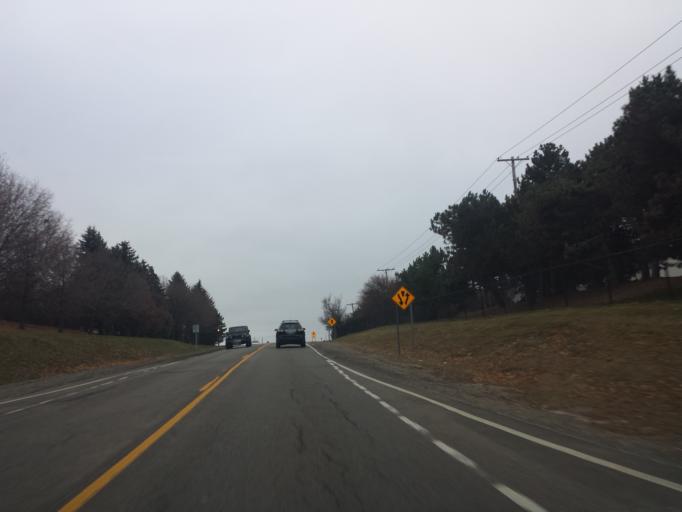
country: US
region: Michigan
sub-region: Oakland County
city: Rochester Hills
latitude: 42.6522
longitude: -83.1928
